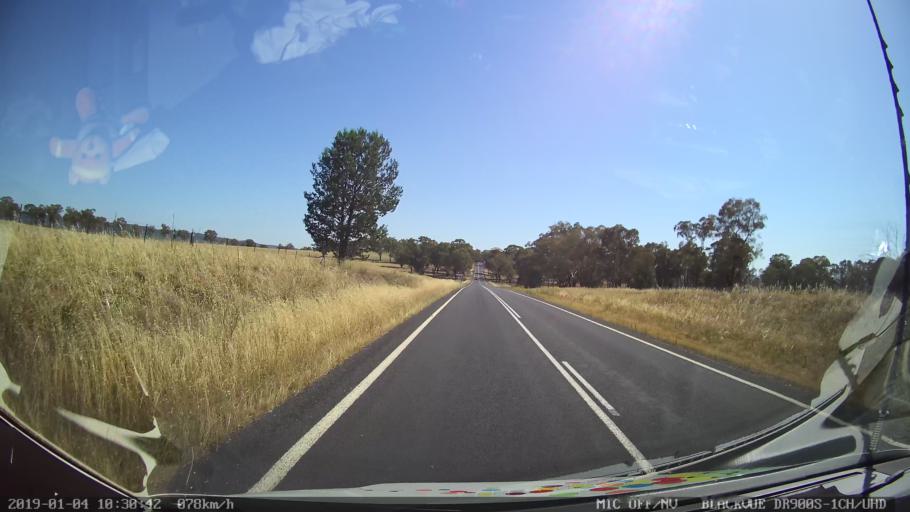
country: AU
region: New South Wales
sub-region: Cabonne
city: Canowindra
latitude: -33.3428
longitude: 148.6292
